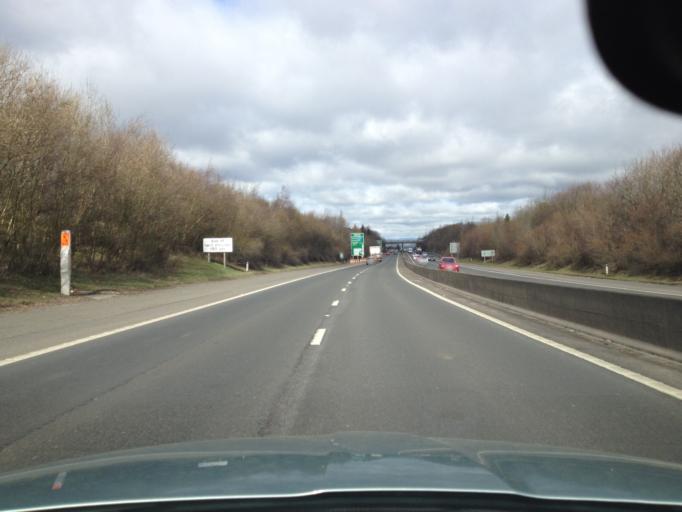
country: GB
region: Scotland
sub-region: Edinburgh
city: Colinton
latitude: 55.9034
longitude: -3.2737
